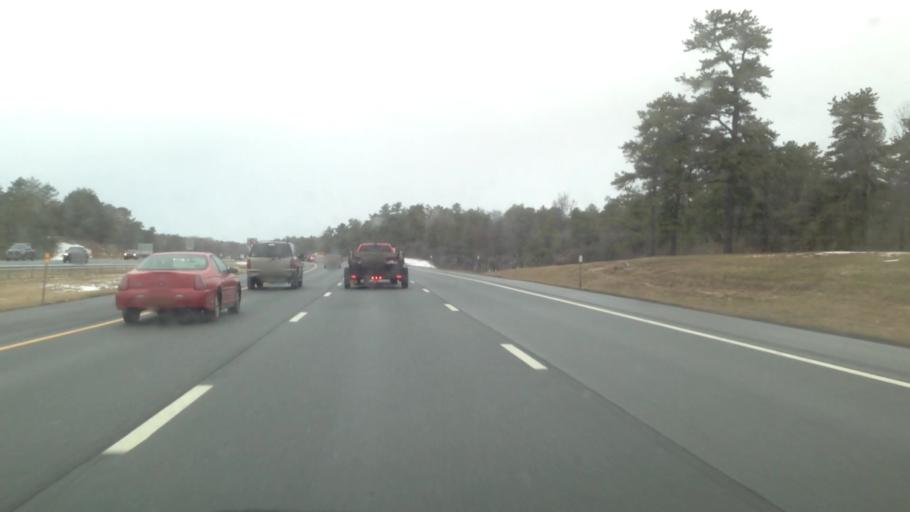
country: US
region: New York
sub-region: Albany County
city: Westmere
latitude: 42.7172
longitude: -73.8733
